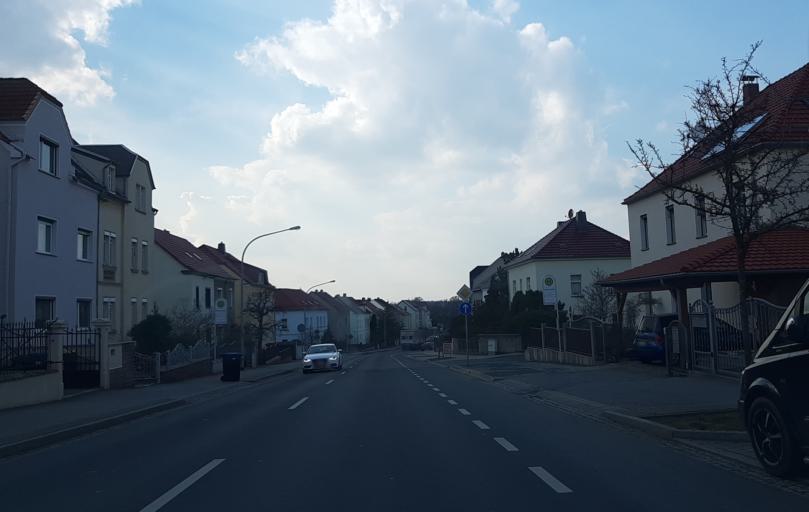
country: DE
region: Saxony
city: Grossenhain
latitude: 51.2859
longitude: 13.5374
